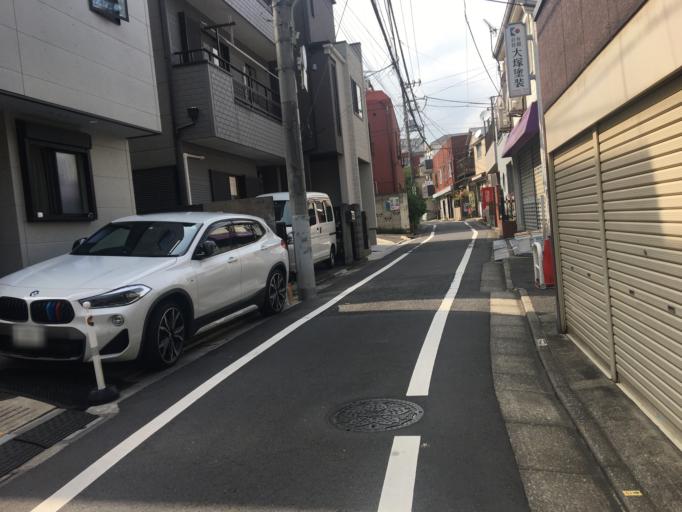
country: JP
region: Tokyo
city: Tokyo
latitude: 35.7396
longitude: 139.7198
